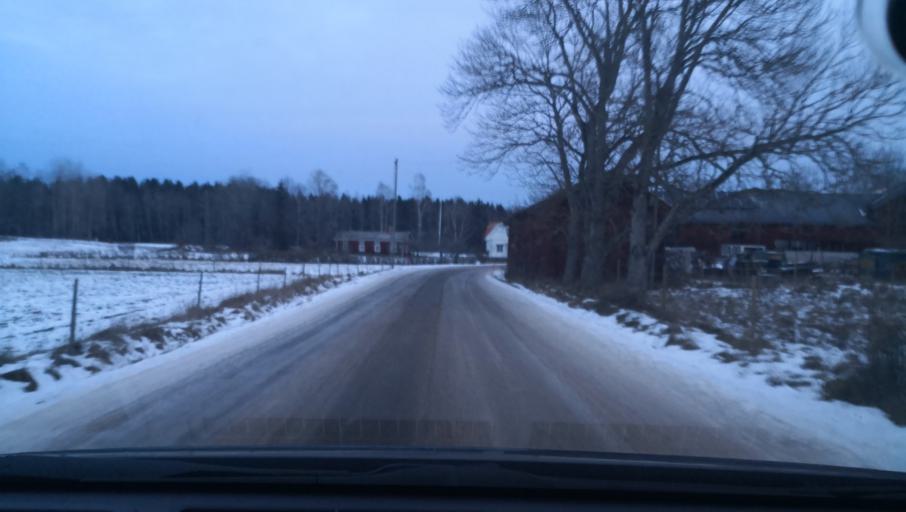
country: SE
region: Dalarna
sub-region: Avesta Kommun
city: Horndal
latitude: 60.1999
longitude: 16.4972
